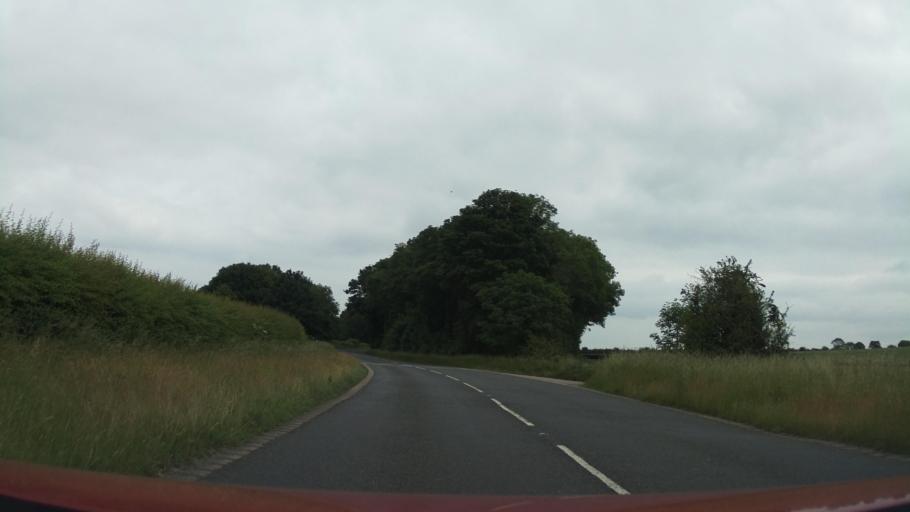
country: GB
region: England
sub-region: District of Rutland
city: Empingham
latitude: 52.6555
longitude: -0.6021
